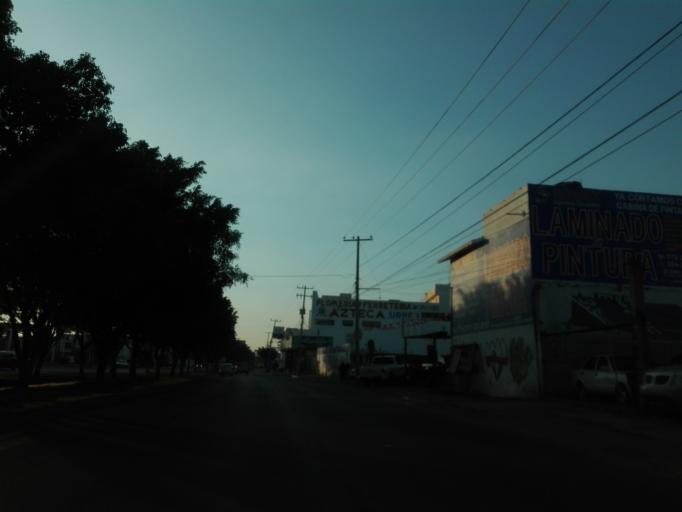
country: MX
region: Guanajuato
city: Leon
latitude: 21.1279
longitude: -101.6433
